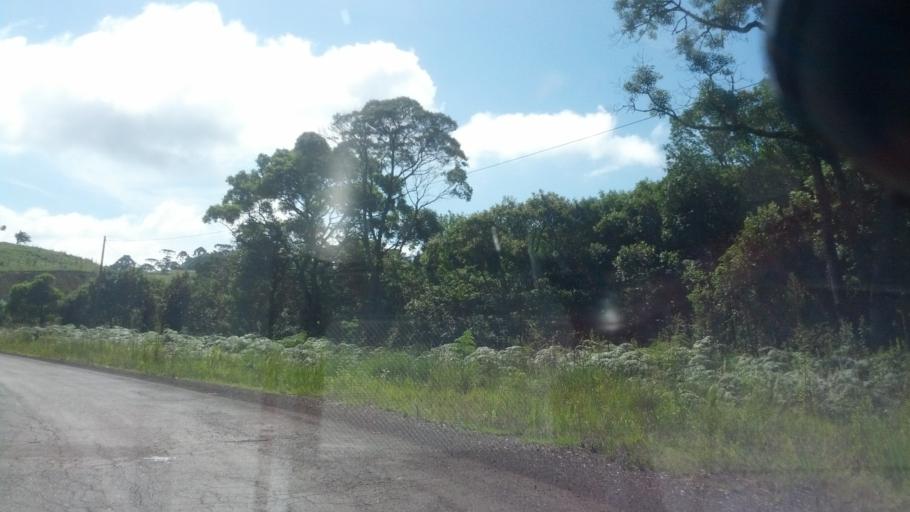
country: BR
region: Santa Catarina
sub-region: Lages
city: Lages
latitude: -27.9499
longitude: -50.5010
